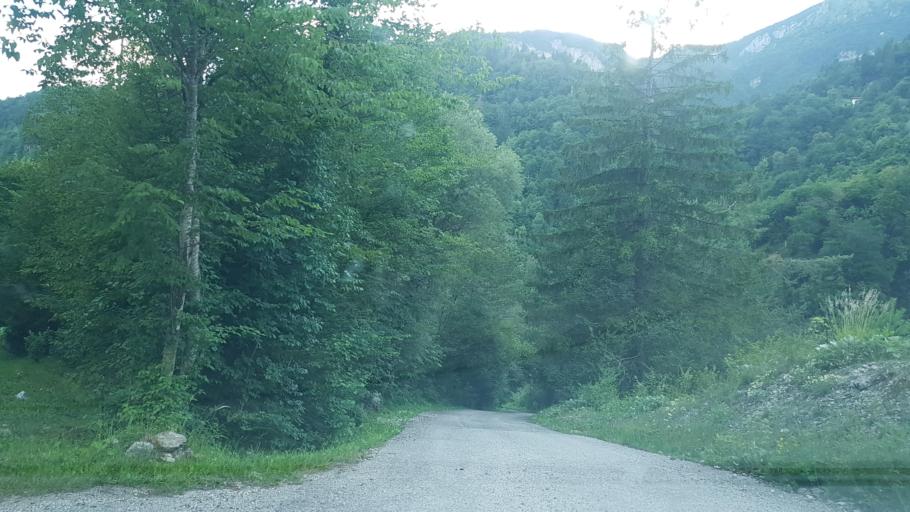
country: IT
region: Friuli Venezia Giulia
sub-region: Provincia di Udine
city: Paularo
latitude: 46.4859
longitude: 13.0993
